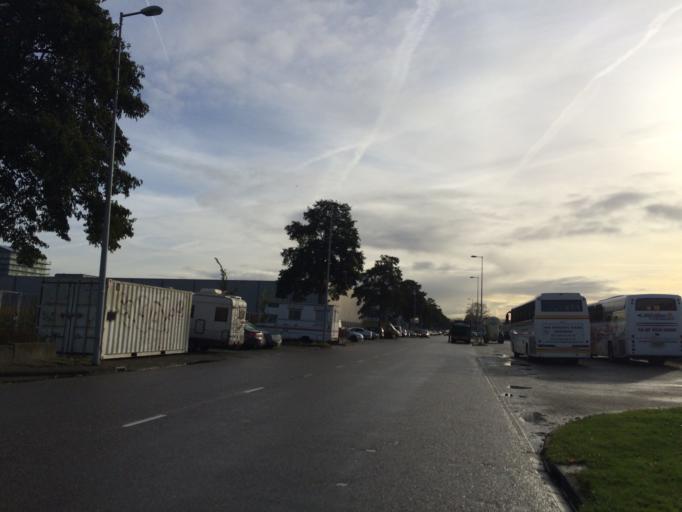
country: NL
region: North Holland
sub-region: Gemeente Amsterdam
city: Amsterdam
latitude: 52.3953
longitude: 4.8991
